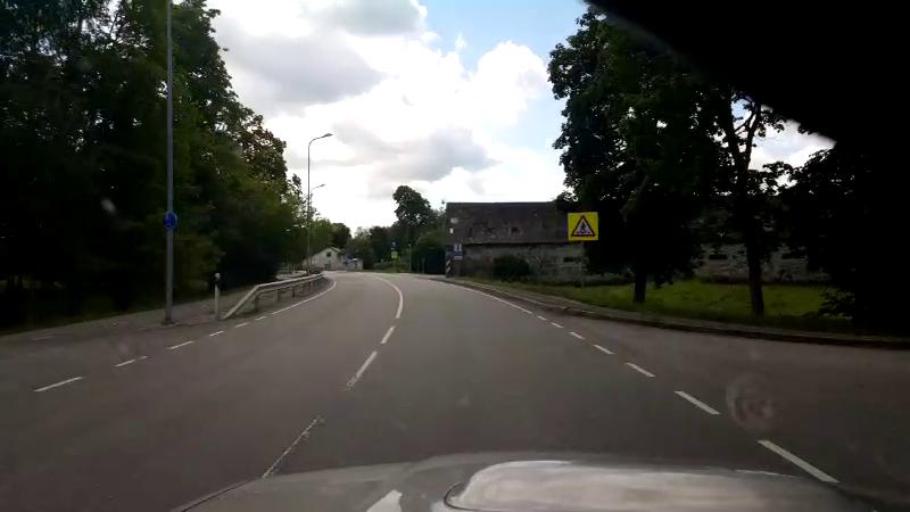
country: EE
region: Jaervamaa
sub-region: Jaerva-Jaani vald
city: Jarva-Jaani
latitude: 59.0304
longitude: 25.7032
